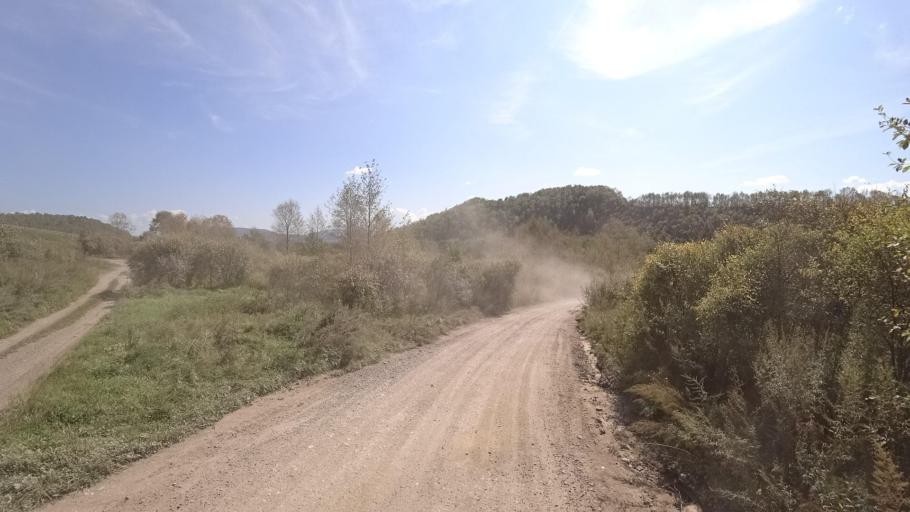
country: RU
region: Jewish Autonomous Oblast
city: Londoko
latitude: 49.0078
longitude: 131.9138
